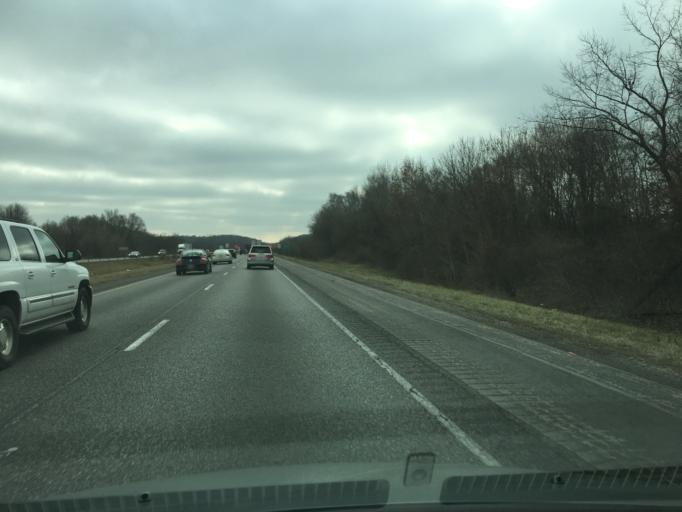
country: US
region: Indiana
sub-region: Tippecanoe County
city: Battle Ground
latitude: 40.4846
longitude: -86.8574
